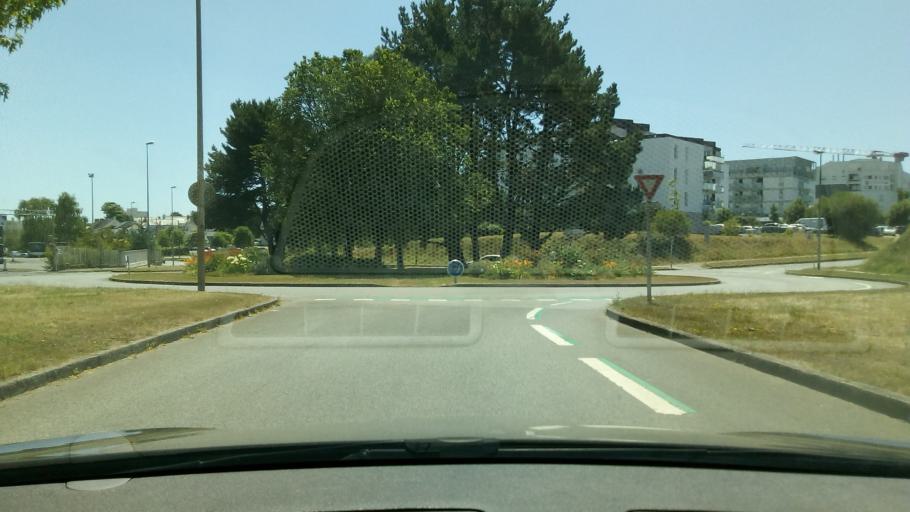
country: FR
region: Brittany
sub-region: Departement du Morbihan
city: Lorient
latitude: 47.7548
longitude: -3.3836
